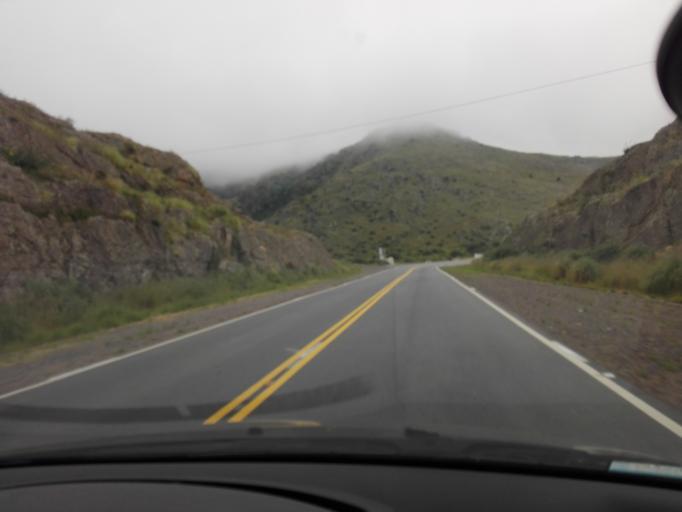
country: AR
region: Cordoba
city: Cuesta Blanca
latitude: -31.6211
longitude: -64.6855
